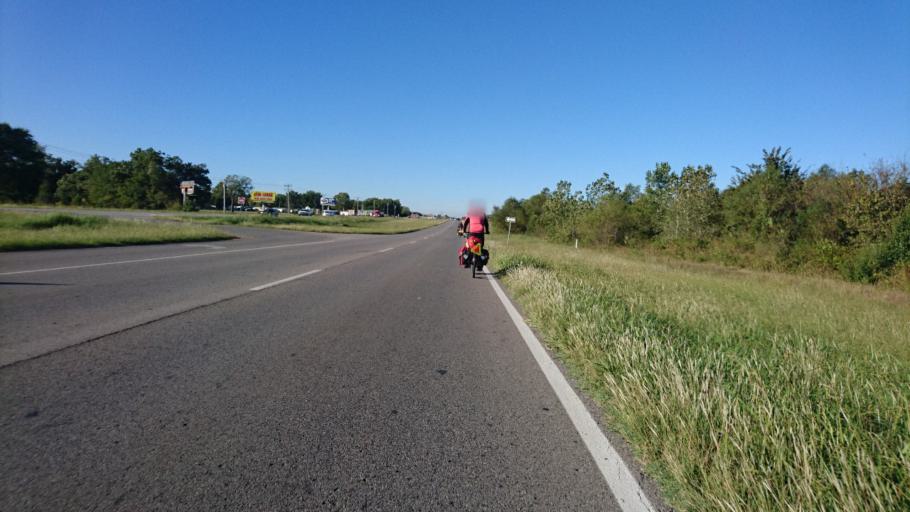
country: US
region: Oklahoma
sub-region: Rogers County
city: Verdigris
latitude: 36.2673
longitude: -95.6497
